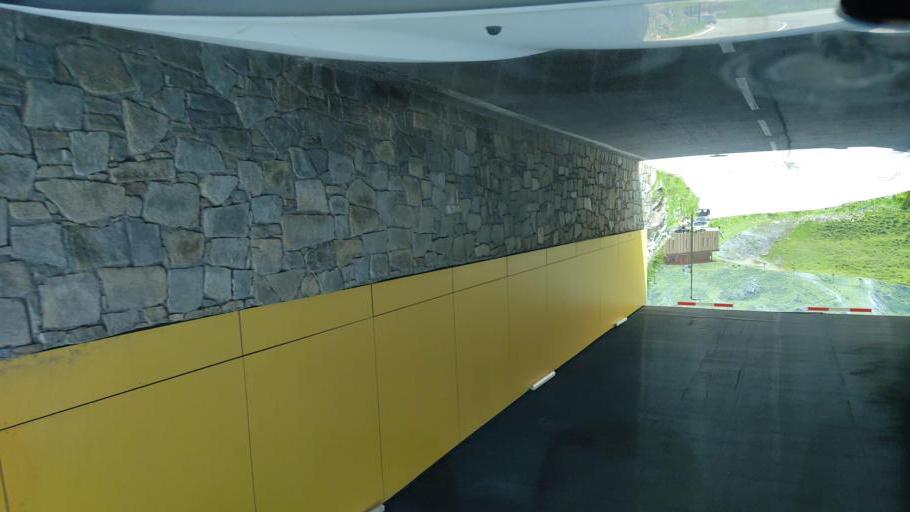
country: FR
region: Rhone-Alpes
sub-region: Departement de la Savoie
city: Seez
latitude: 45.5729
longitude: 6.8338
